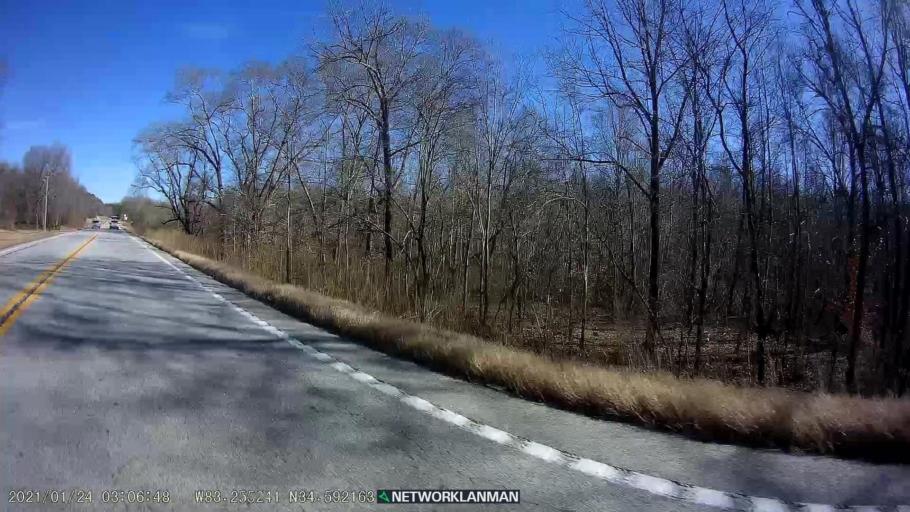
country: US
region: Georgia
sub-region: Stephens County
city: Toccoa
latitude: 34.5924
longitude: -83.2546
